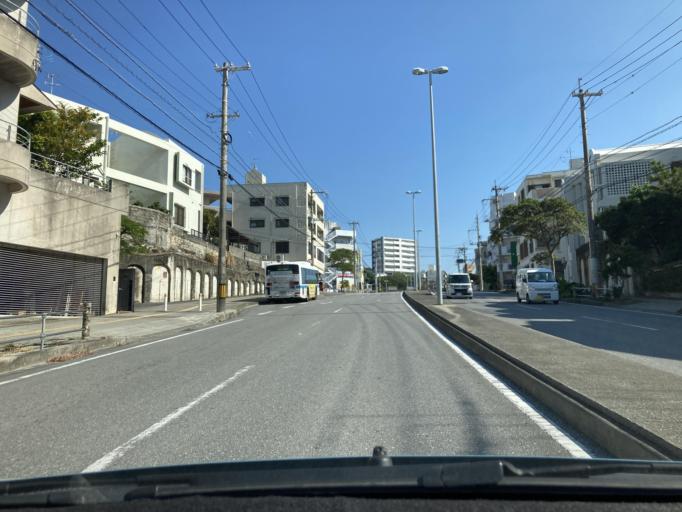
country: JP
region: Okinawa
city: Naha-shi
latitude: 26.2042
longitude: 127.7052
